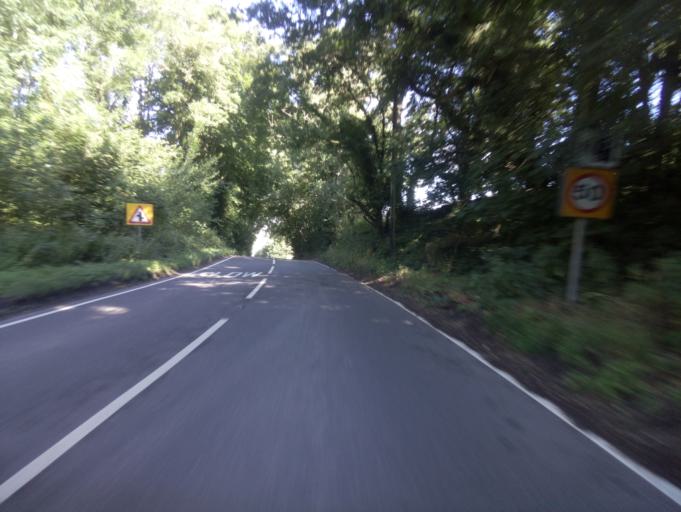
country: GB
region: England
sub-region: Herefordshire
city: Yatton
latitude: 51.9758
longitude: -2.5554
